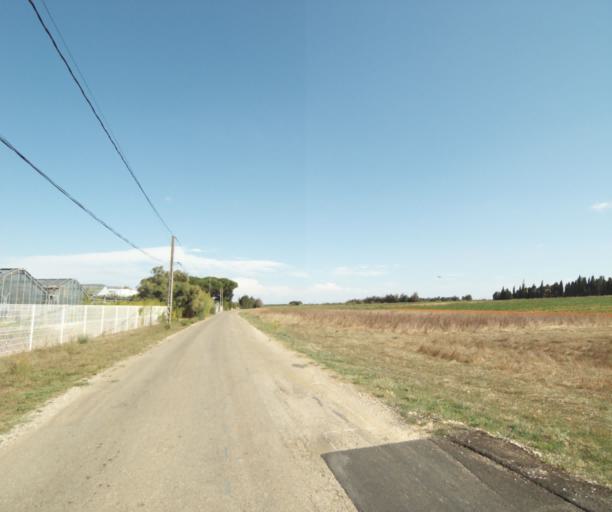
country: FR
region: Languedoc-Roussillon
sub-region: Departement du Gard
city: Manduel
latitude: 43.7995
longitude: 4.4613
